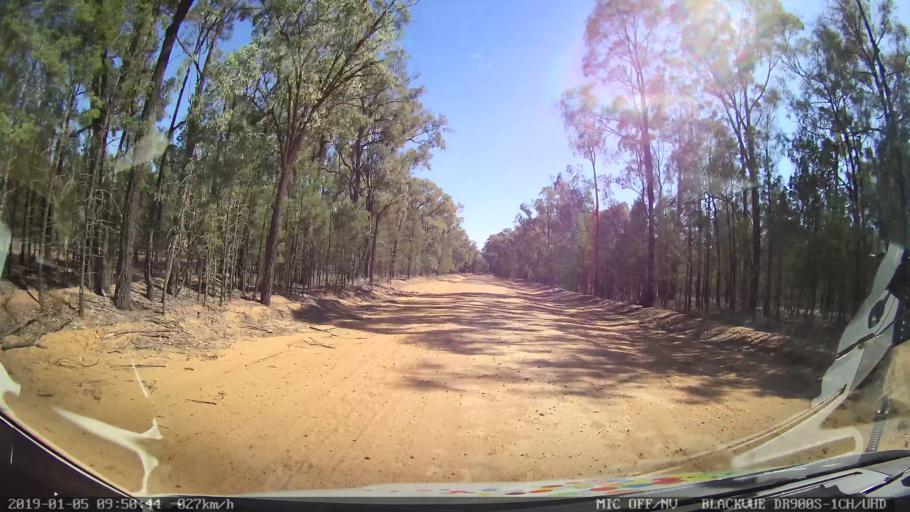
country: AU
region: New South Wales
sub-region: Gilgandra
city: Gilgandra
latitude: -31.6634
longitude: 148.7591
